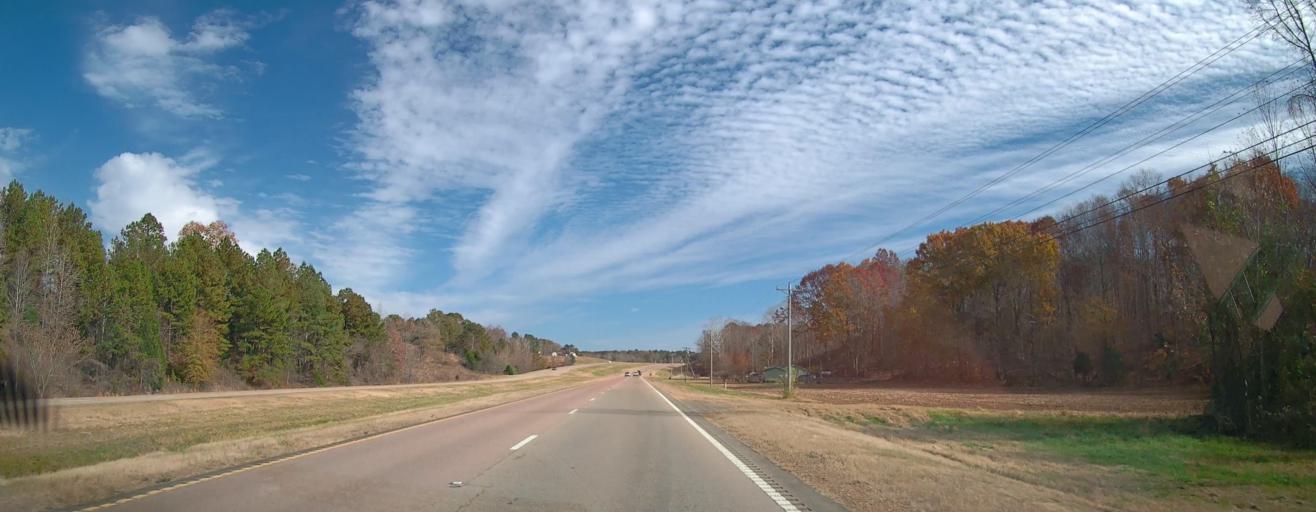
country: US
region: Mississippi
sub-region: Tippah County
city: Ripley
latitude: 34.9550
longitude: -88.8588
